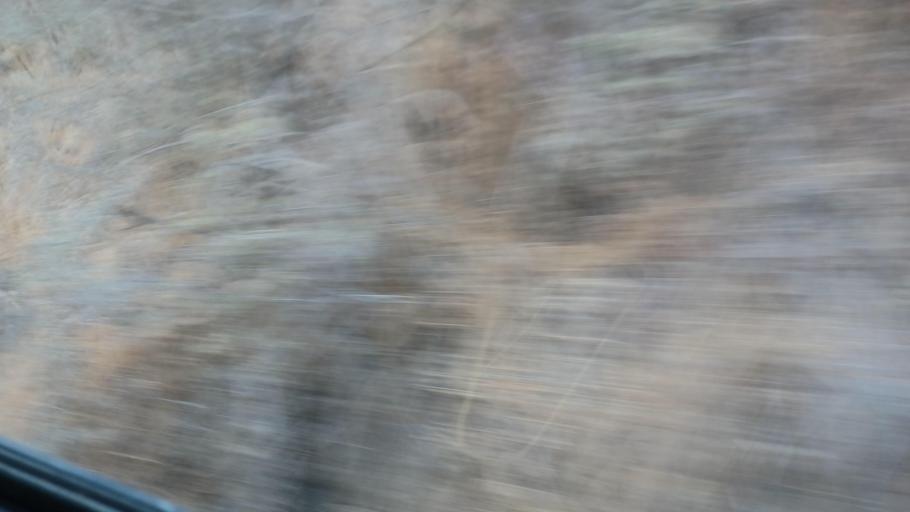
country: CY
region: Pafos
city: Tala
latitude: 34.9271
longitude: 32.4820
